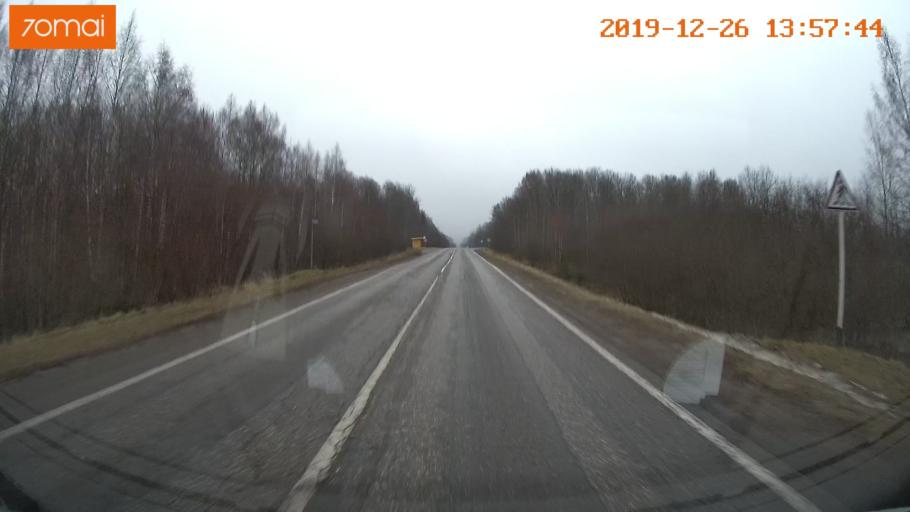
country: RU
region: Jaroslavl
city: Poshekhon'ye
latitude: 58.5798
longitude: 38.6857
